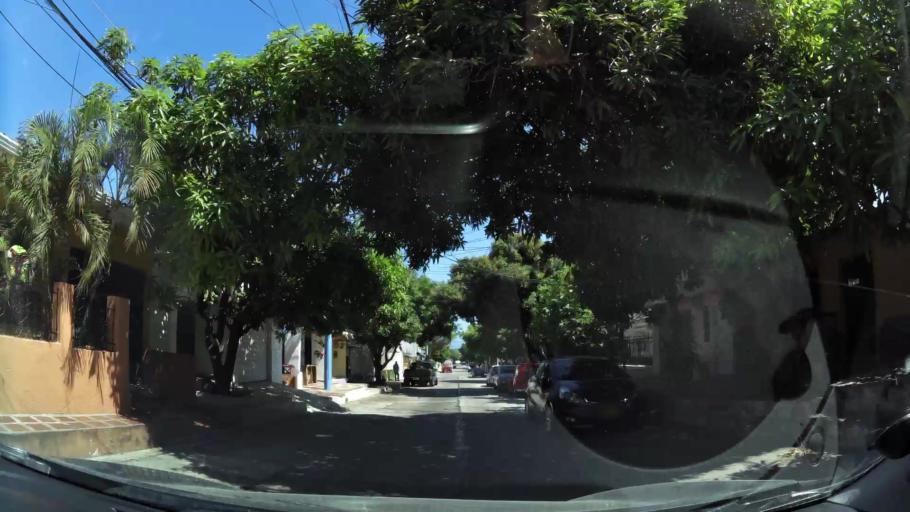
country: CO
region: Atlantico
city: Barranquilla
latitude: 11.0030
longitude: -74.7936
